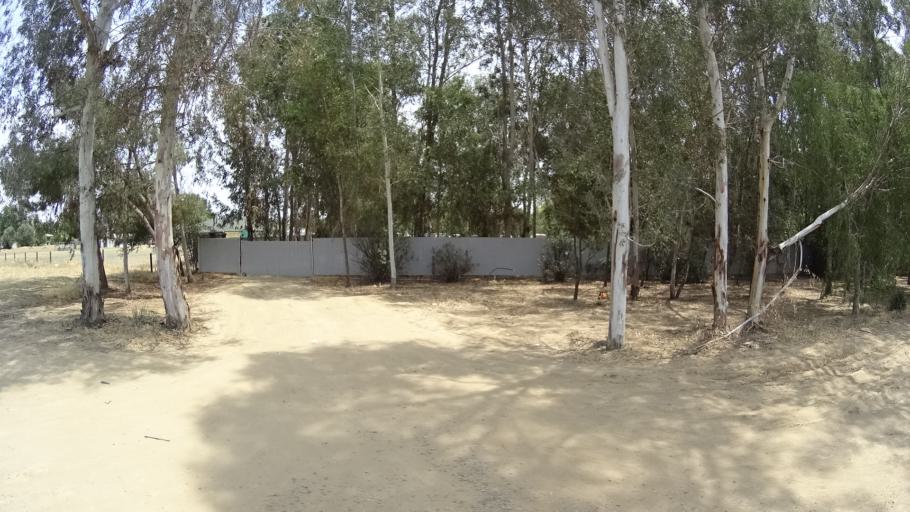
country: US
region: California
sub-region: Fresno County
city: Sunnyside
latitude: 36.7481
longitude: -119.6640
